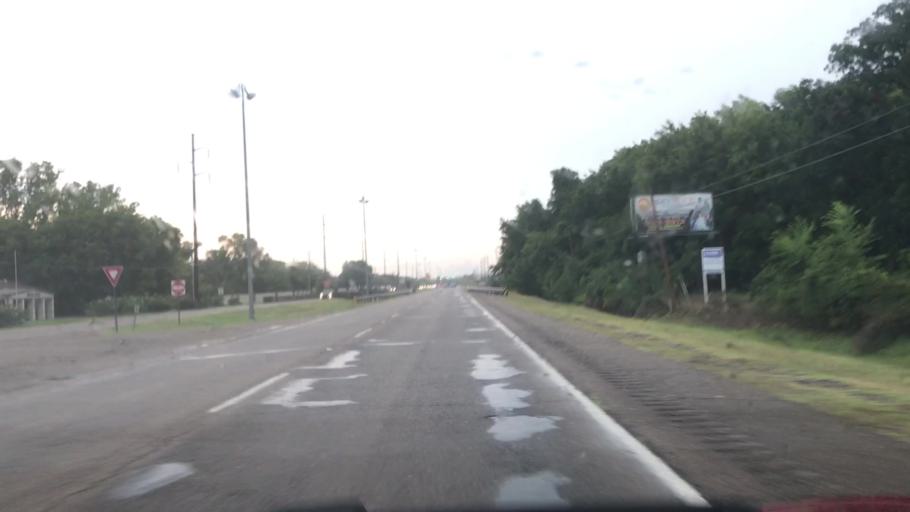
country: US
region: Louisiana
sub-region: Bossier Parish
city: Red Chute
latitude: 32.5395
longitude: -93.6532
